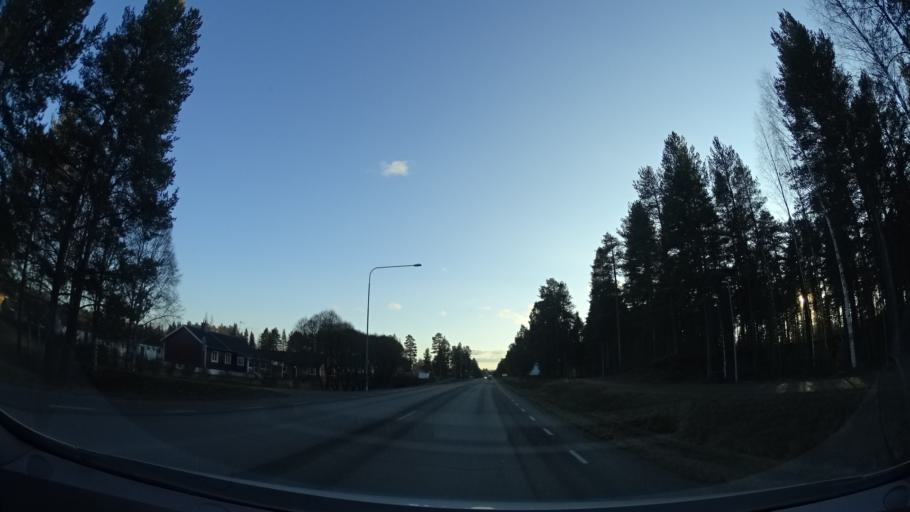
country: SE
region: Vaesterbotten
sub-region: Lycksele Kommun
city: Lycksele
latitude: 64.6020
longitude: 18.7006
